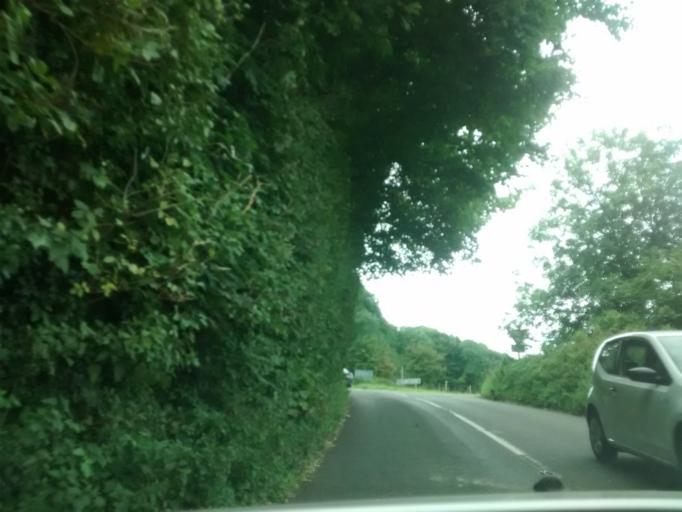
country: GB
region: England
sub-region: South Gloucestershire
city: Cold Ashton
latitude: 51.4330
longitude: -2.3994
